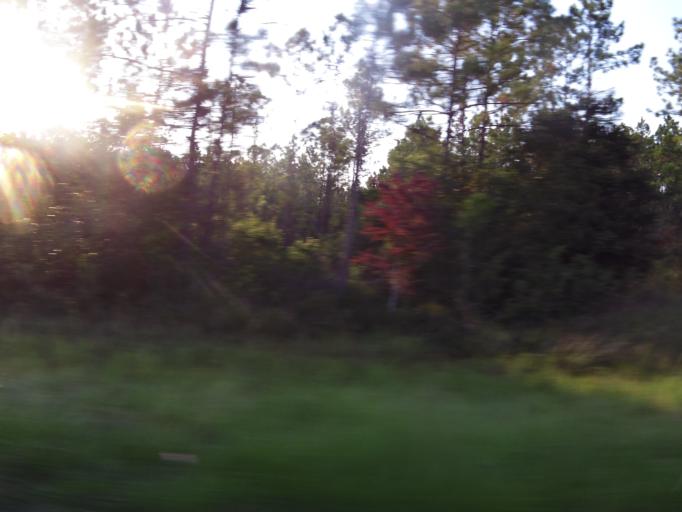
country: US
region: Florida
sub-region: Baker County
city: Macclenny
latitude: 30.4407
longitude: -82.0815
